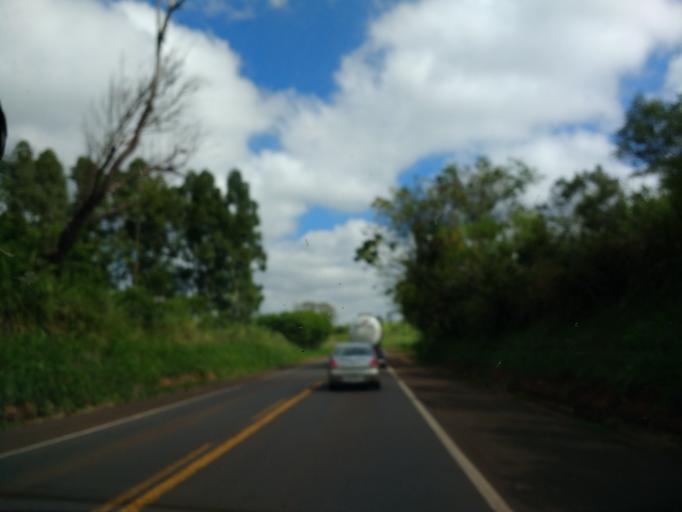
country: BR
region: Parana
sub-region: Cruzeiro Do Oeste
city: Cruzeiro do Oeste
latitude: -23.7647
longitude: -53.0050
